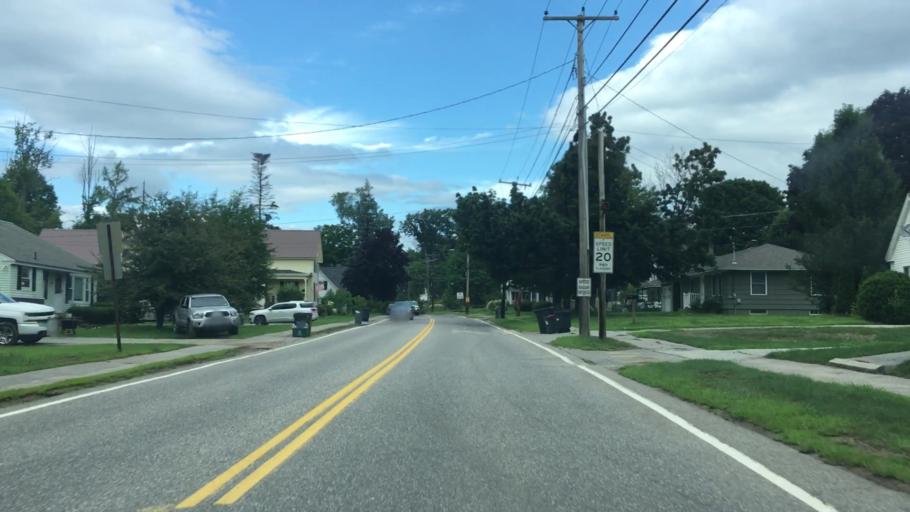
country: US
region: New Hampshire
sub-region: Belknap County
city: Laconia
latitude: 43.5565
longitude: -71.4703
